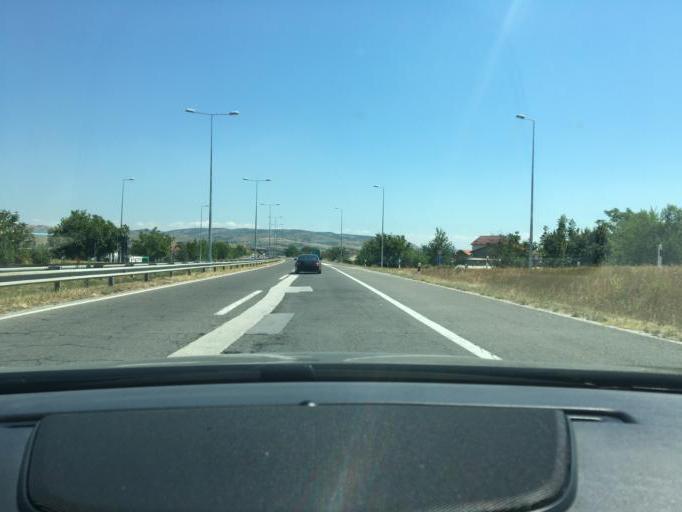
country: MK
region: Ilinden
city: Ilinden
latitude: 41.9967
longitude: 21.5556
